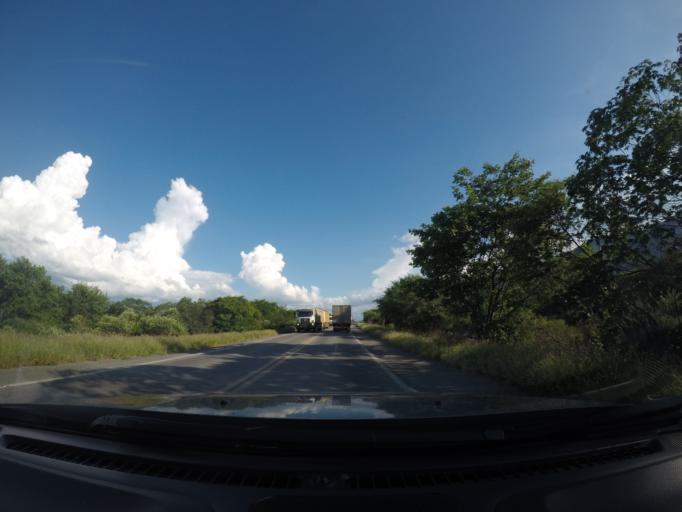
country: BR
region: Bahia
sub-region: Oliveira Dos Brejinhos
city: Oliveira dos Brejinhos
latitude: -12.0432
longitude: -42.9732
